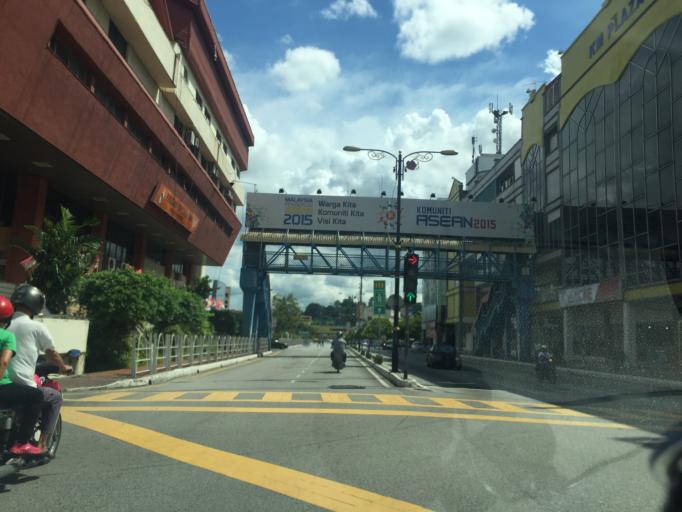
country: MY
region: Negeri Sembilan
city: Seremban
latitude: 2.7238
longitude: 101.9376
